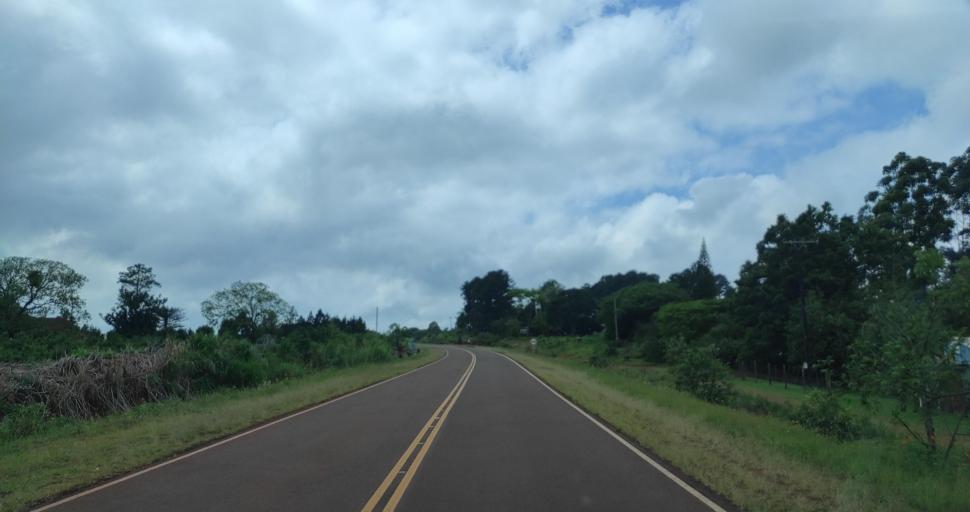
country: AR
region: Misiones
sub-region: Departamento de Veinticinco de Mayo
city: Veinticinco de Mayo
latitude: -27.3399
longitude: -54.8856
